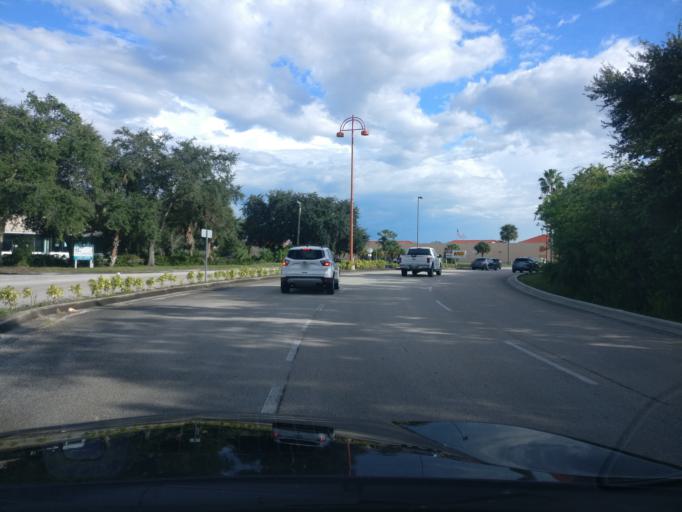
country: US
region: Florida
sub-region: Indian River County
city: West Vero Corridor
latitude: 27.6385
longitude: -80.5227
